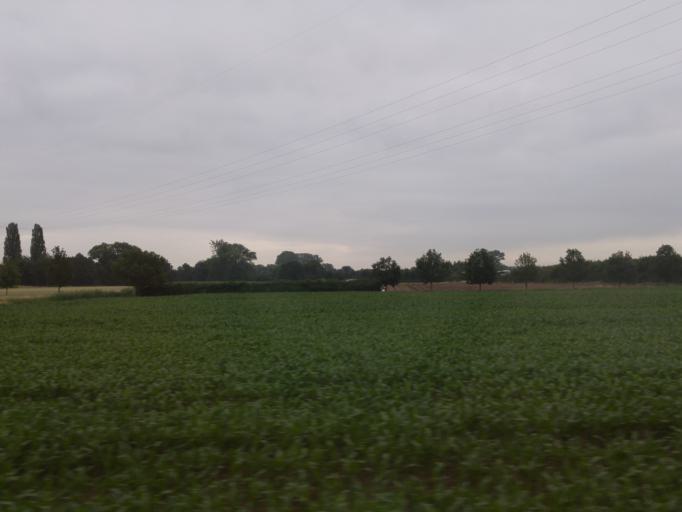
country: DE
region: Hesse
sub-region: Regierungsbezirk Darmstadt
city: Erzhausen
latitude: 49.9221
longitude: 8.6467
